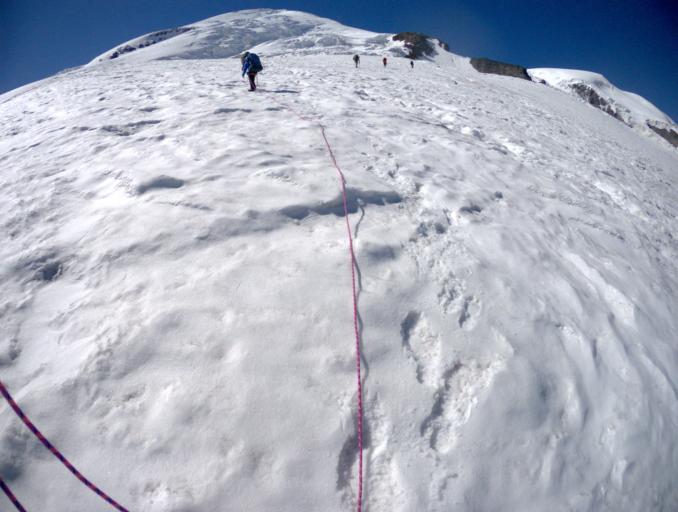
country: RU
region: Kabardino-Balkariya
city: Terskol
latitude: 43.3845
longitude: 42.4371
